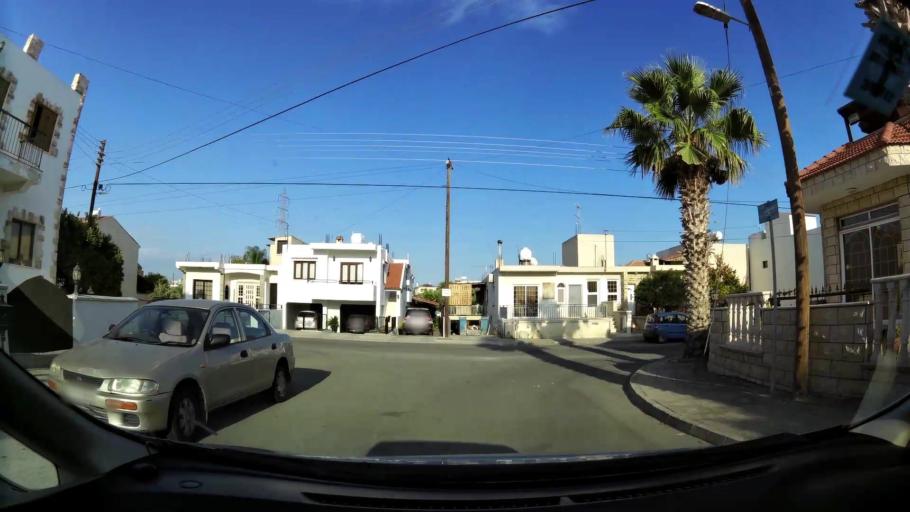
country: CY
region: Larnaka
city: Aradippou
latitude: 34.9331
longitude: 33.6035
